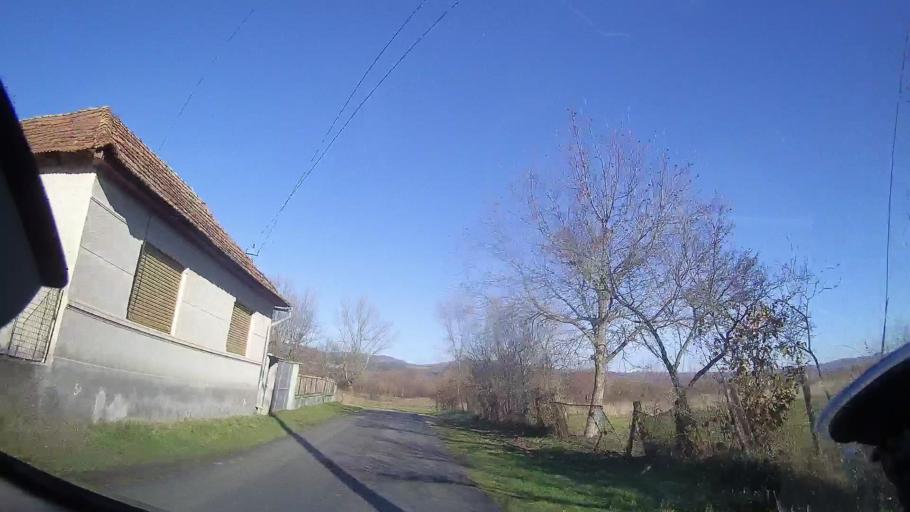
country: RO
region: Bihor
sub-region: Comuna Auseu
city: Auseu
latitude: 47.0210
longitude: 22.4948
